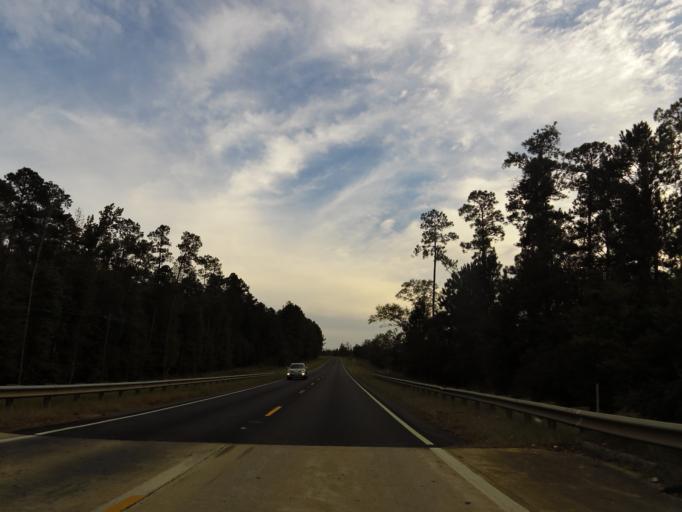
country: US
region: Alabama
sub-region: Monroe County
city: Frisco City
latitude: 31.2548
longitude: -87.4927
